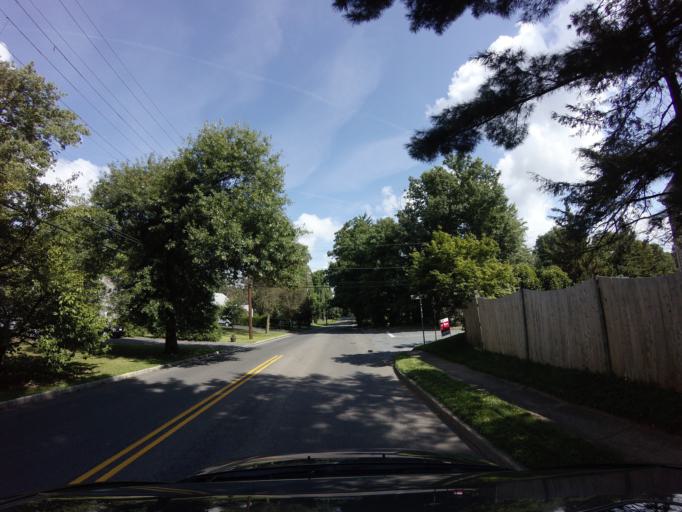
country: US
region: New Jersey
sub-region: Morris County
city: Chatham
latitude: 40.7206
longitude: -74.3844
